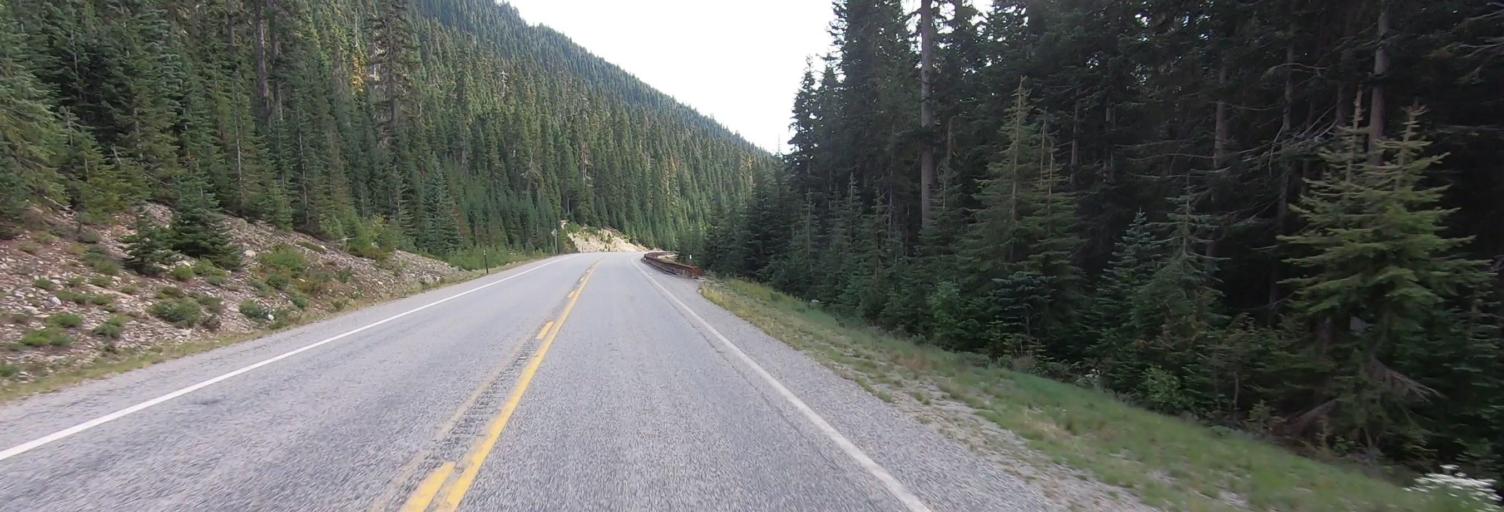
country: US
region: Washington
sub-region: Chelan County
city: Granite Falls
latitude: 48.5252
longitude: -120.7375
